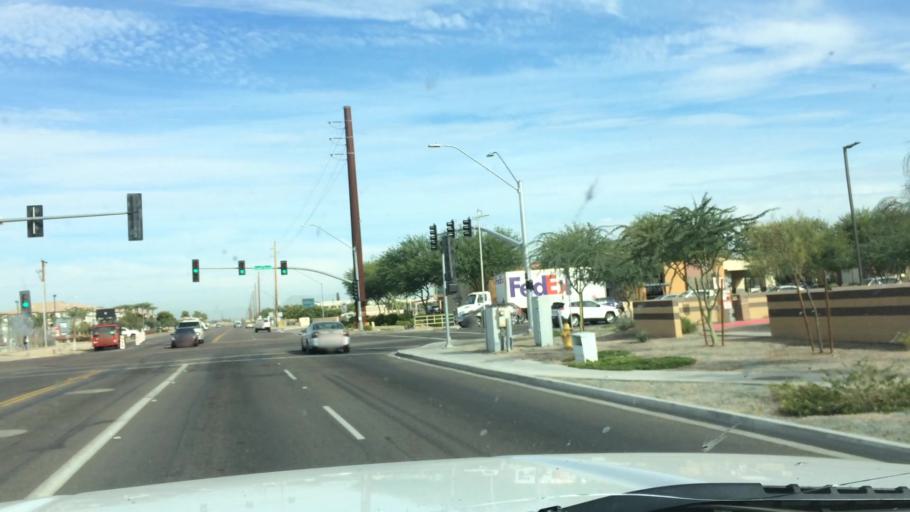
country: US
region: Arizona
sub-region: Maricopa County
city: Tolleson
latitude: 33.5078
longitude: -112.2725
